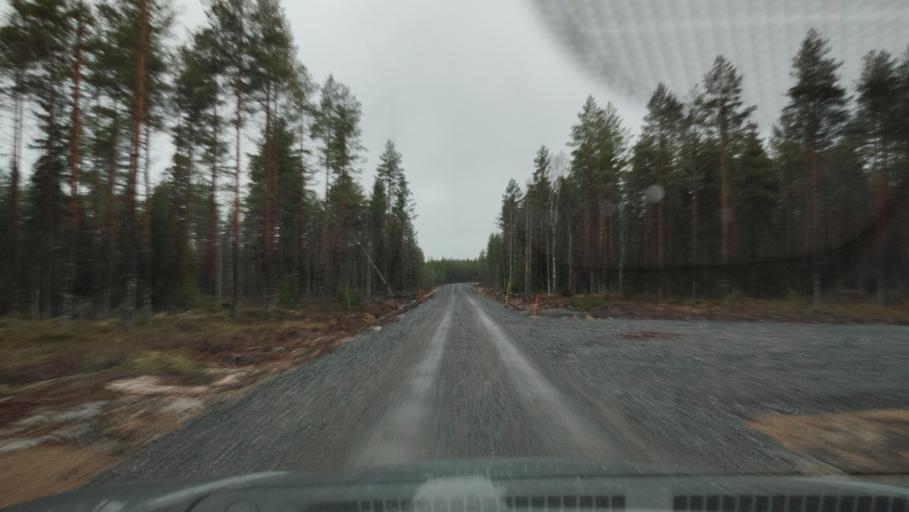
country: FI
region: Southern Ostrobothnia
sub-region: Suupohja
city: Karijoki
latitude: 62.1451
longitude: 21.6134
